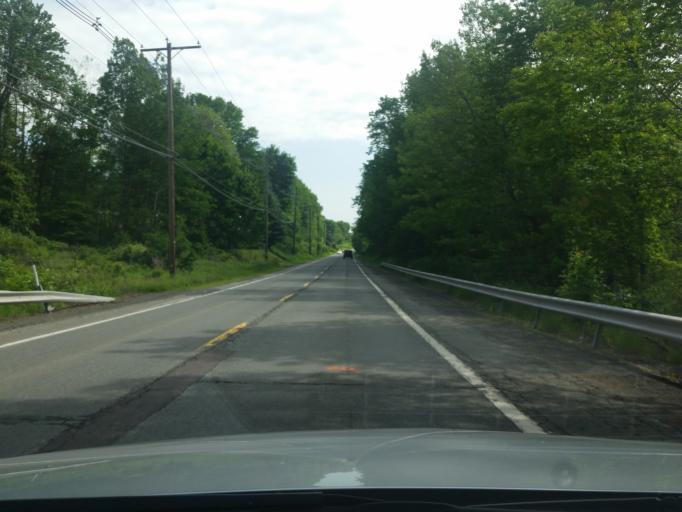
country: US
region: Pennsylvania
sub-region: Luzerne County
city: Back Mountain
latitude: 41.3200
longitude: -76.0176
